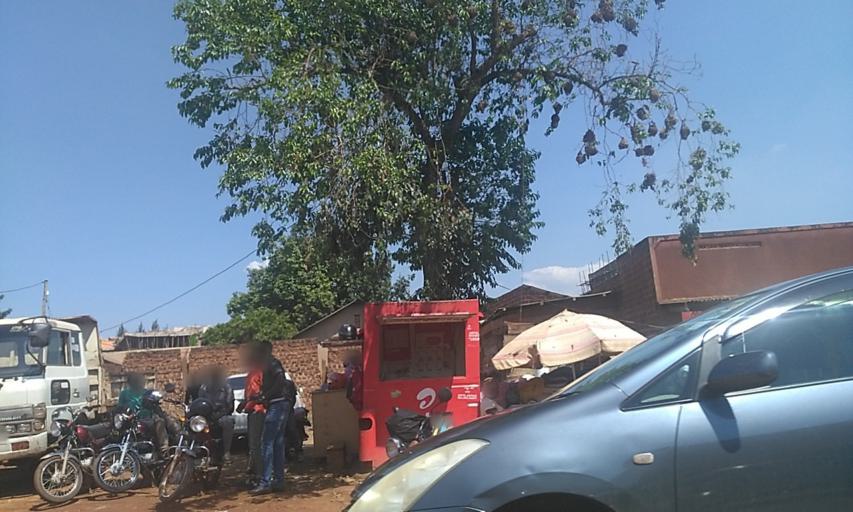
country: UG
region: Central Region
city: Kampala Central Division
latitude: 0.3891
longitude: 32.5929
